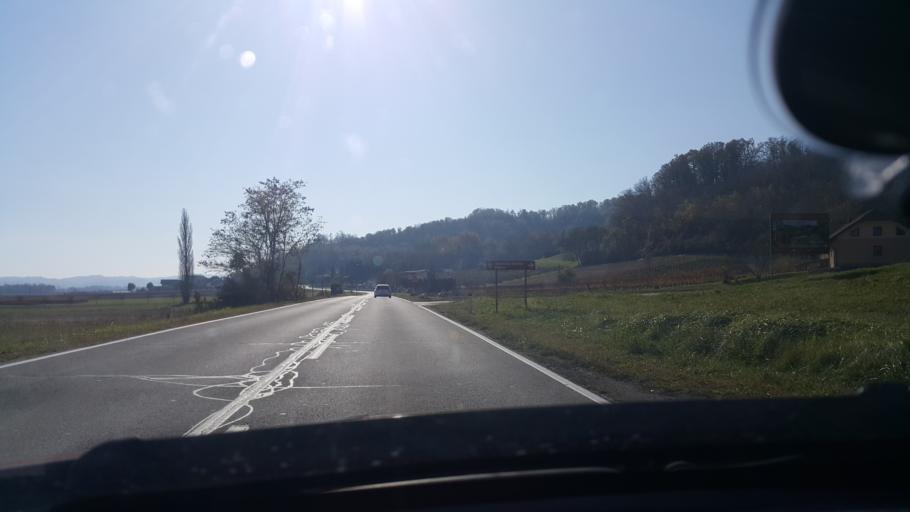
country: SI
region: Bistrica ob Sotli
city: Bistrica ob Sotli
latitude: 45.9939
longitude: 15.6951
